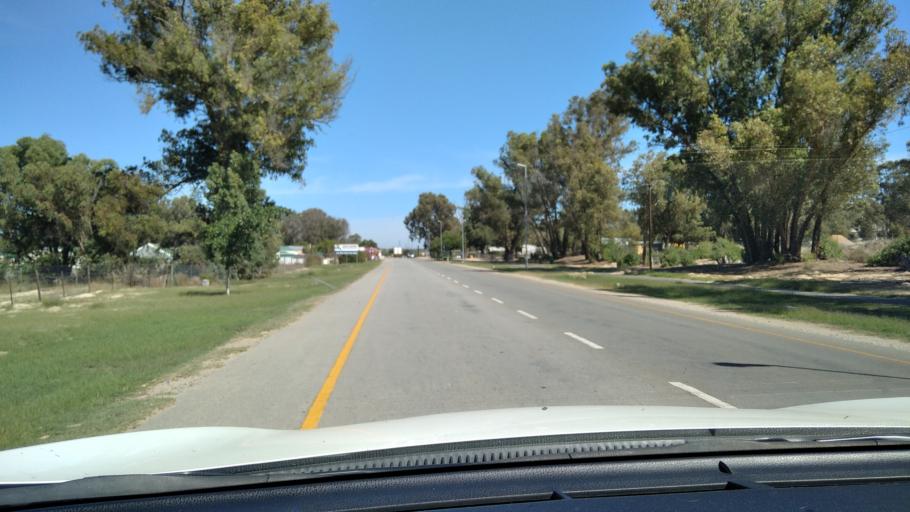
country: ZA
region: Western Cape
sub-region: West Coast District Municipality
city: Moorreesburg
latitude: -33.0576
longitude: 18.3427
